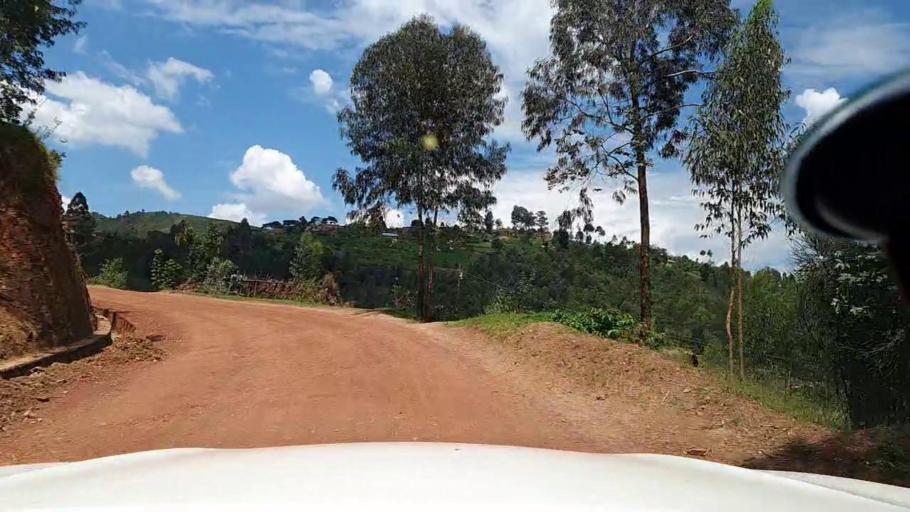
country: RW
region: Northern Province
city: Byumba
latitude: -1.7366
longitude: 29.8614
